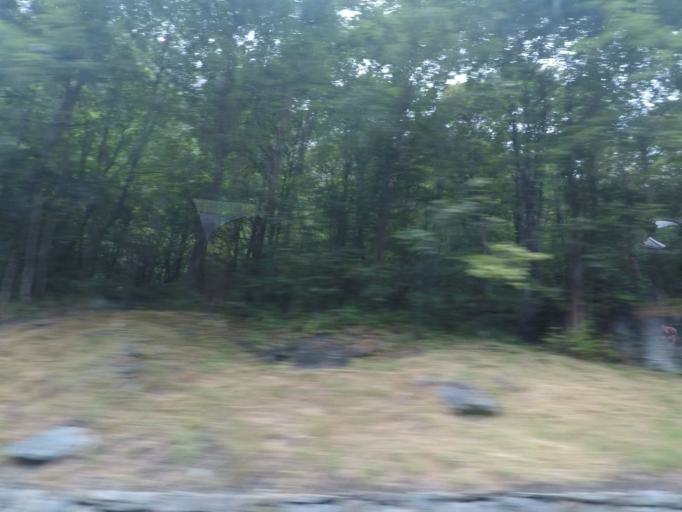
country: IT
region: Aosta Valley
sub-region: Valle d'Aosta
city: Chamois
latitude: 45.8405
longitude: 7.6044
